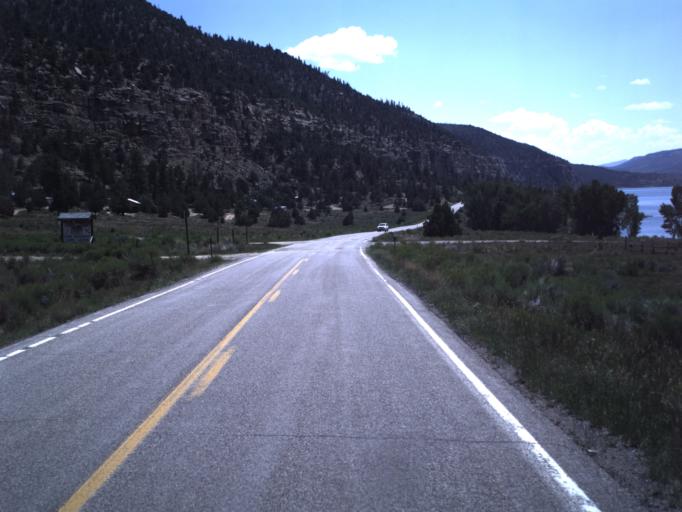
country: US
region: Utah
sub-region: Emery County
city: Orangeville
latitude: 39.3092
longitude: -111.2737
